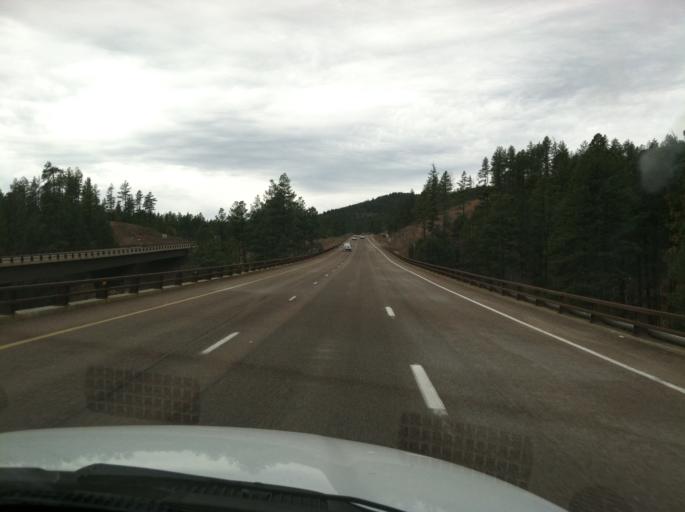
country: US
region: Arizona
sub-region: Gila County
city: Star Valley
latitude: 34.3294
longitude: -111.0930
